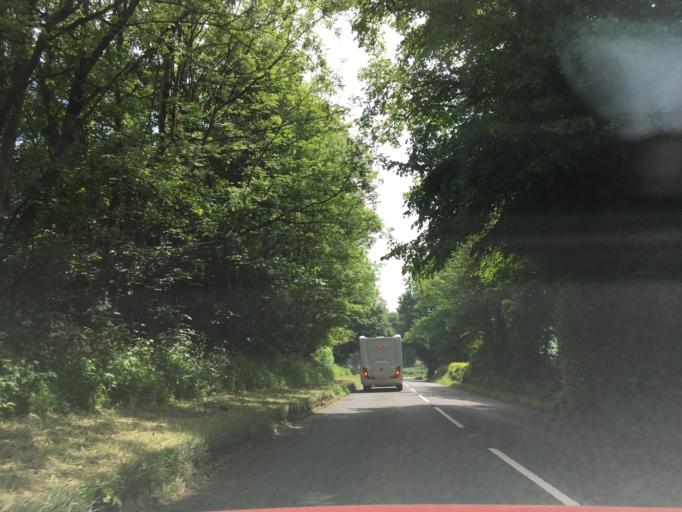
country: GB
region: England
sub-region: Devon
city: Totnes
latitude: 50.4041
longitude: -3.7124
